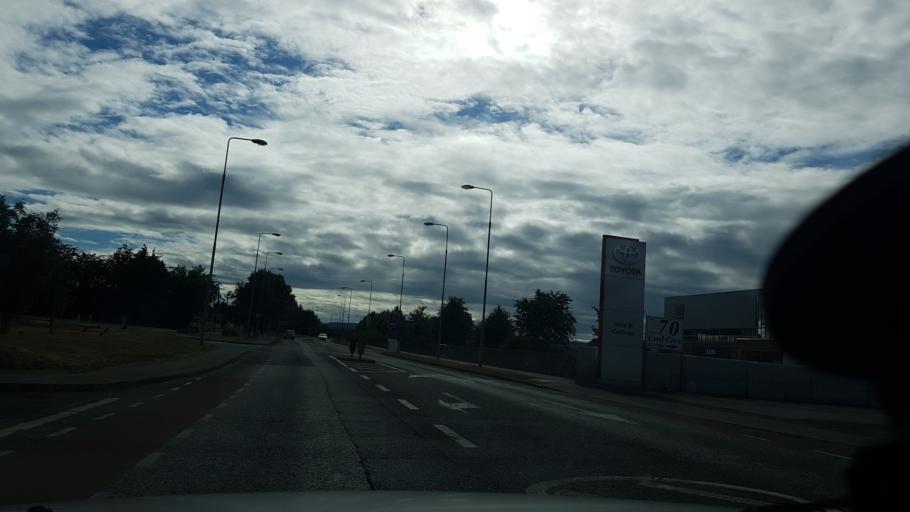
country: IE
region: Munster
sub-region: North Tipperary
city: Nenagh
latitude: 52.8612
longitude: -8.2155
